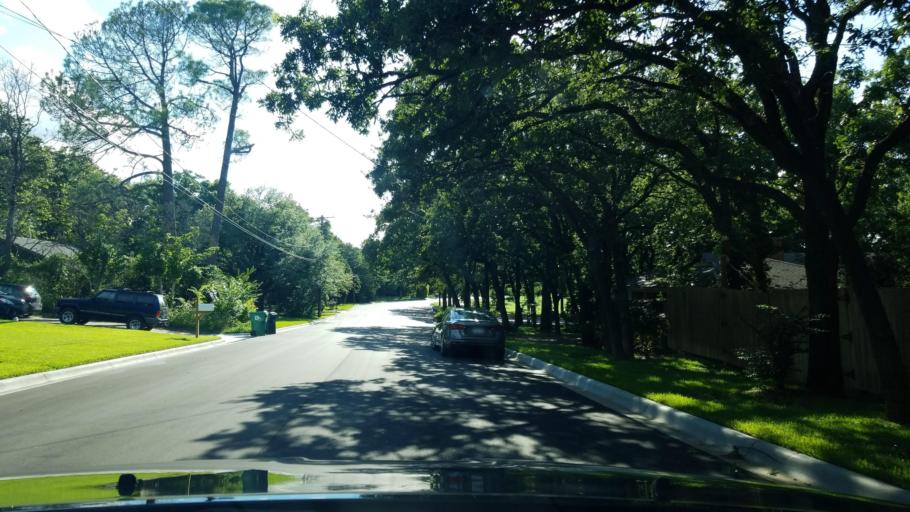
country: US
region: Texas
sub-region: Denton County
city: Denton
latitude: 33.2372
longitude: -97.1120
